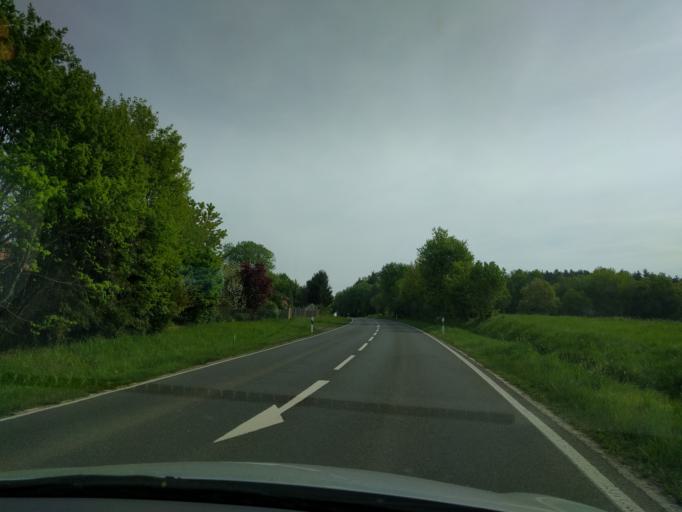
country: DE
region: Bavaria
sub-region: Upper Palatinate
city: Schorndorf
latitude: 49.1828
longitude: 12.6322
